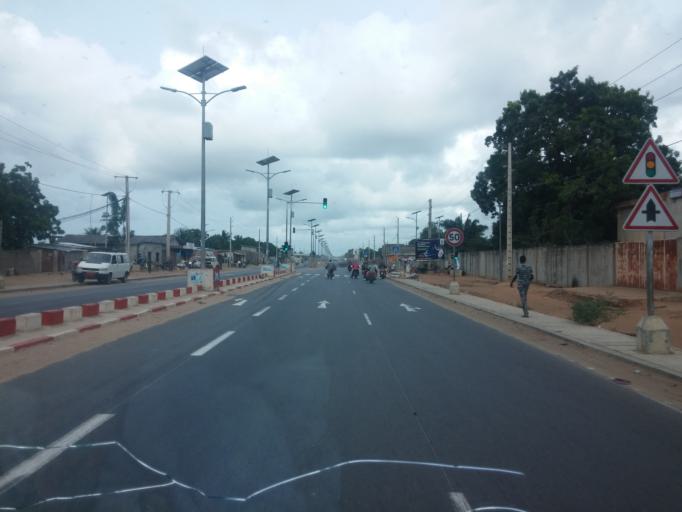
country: BJ
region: Atlantique
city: Hevie
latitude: 6.3868
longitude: 2.2271
